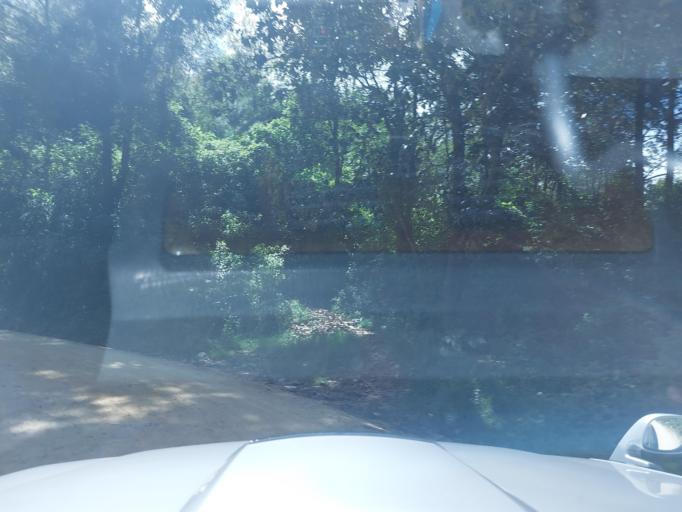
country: GT
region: Chimaltenango
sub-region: Municipio de San Juan Comalapa
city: Comalapa
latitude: 14.7605
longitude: -90.8816
